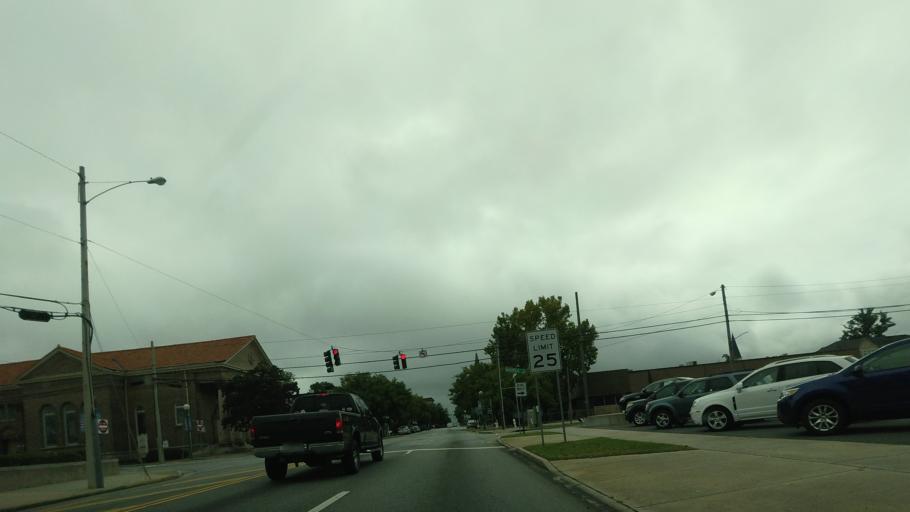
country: US
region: Georgia
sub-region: Lowndes County
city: Valdosta
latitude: 30.8344
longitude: -83.2808
